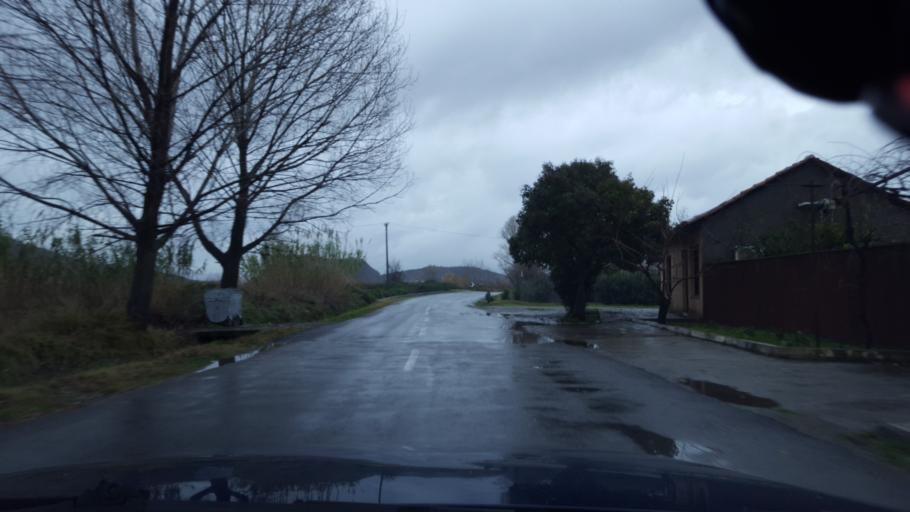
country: AL
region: Shkoder
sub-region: Rrethi i Shkodres
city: Berdica e Madhe
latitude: 42.0251
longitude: 19.4876
